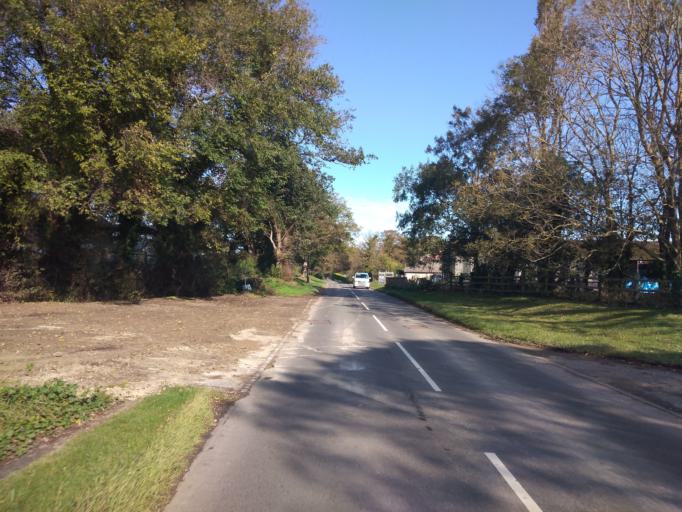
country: GB
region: England
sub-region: East Sussex
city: Seaford
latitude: 50.8192
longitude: 0.1628
